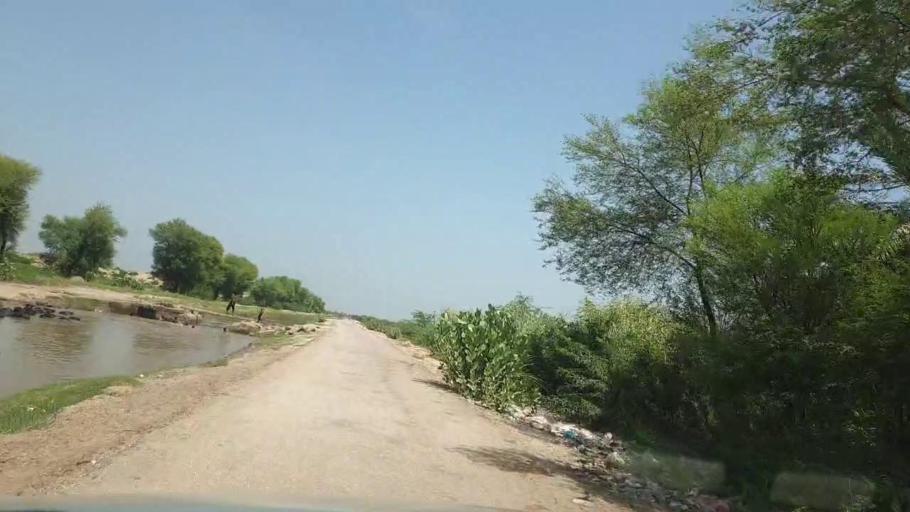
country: PK
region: Sindh
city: Rohri
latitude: 27.6165
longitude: 69.0991
